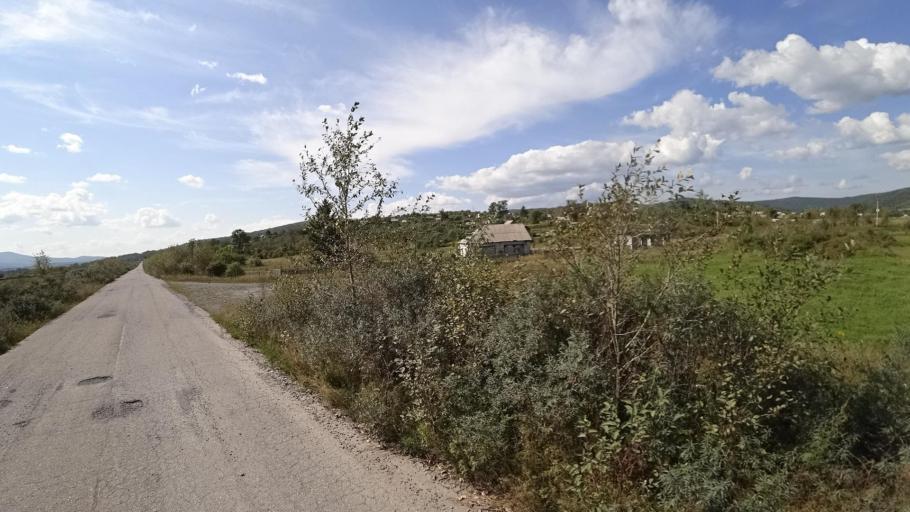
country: RU
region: Jewish Autonomous Oblast
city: Londoko
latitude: 49.0050
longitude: 131.8761
